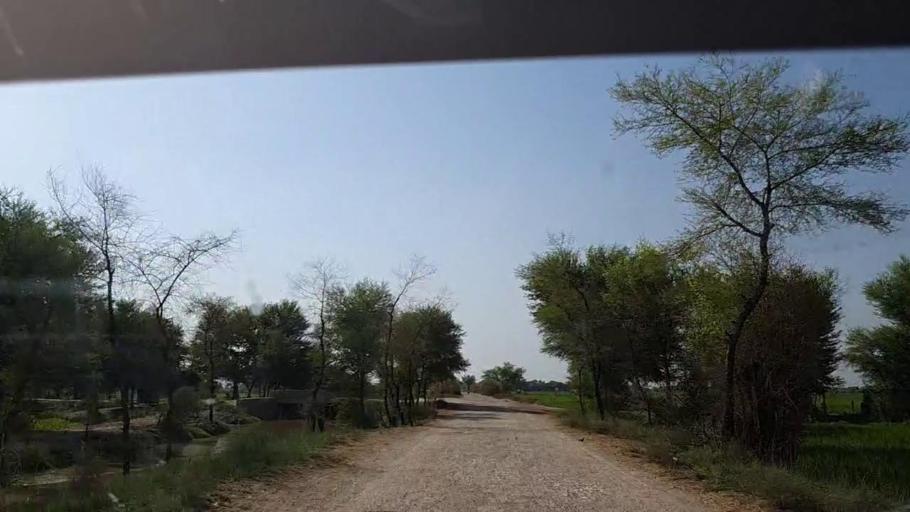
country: PK
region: Sindh
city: Ghauspur
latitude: 28.2038
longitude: 69.0364
